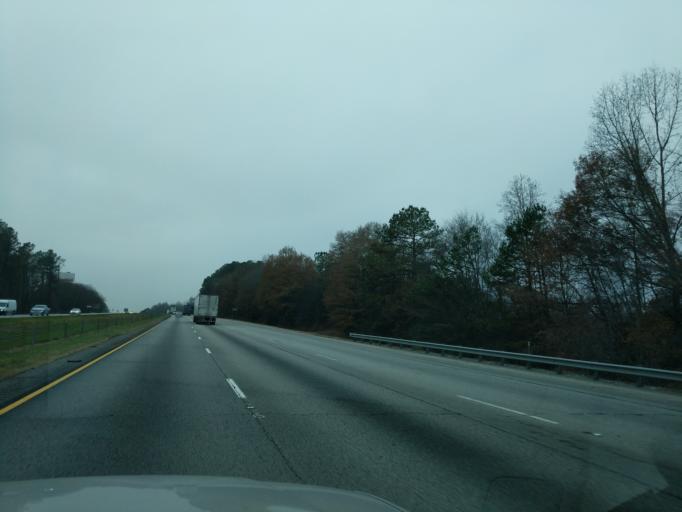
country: US
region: Georgia
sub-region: Franklin County
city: Carnesville
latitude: 34.3460
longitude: -83.3204
